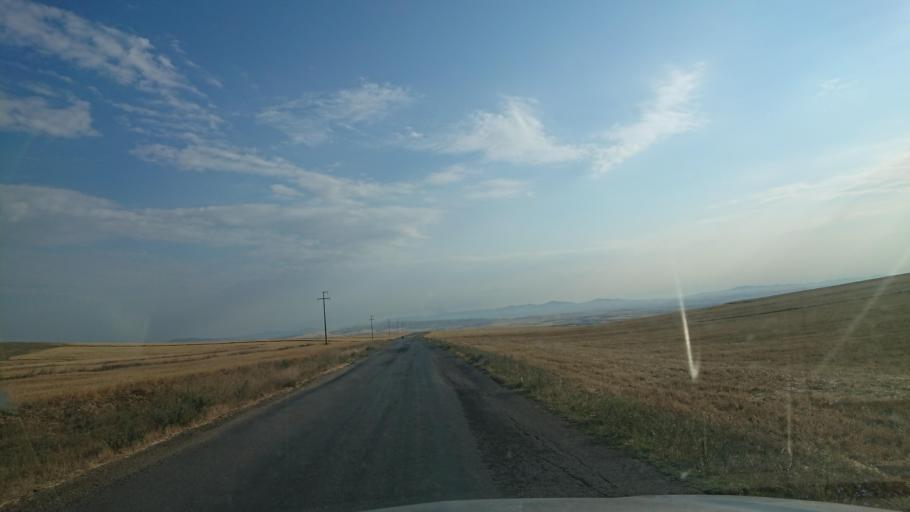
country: TR
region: Aksaray
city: Ortakoy
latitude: 38.7796
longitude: 34.0610
